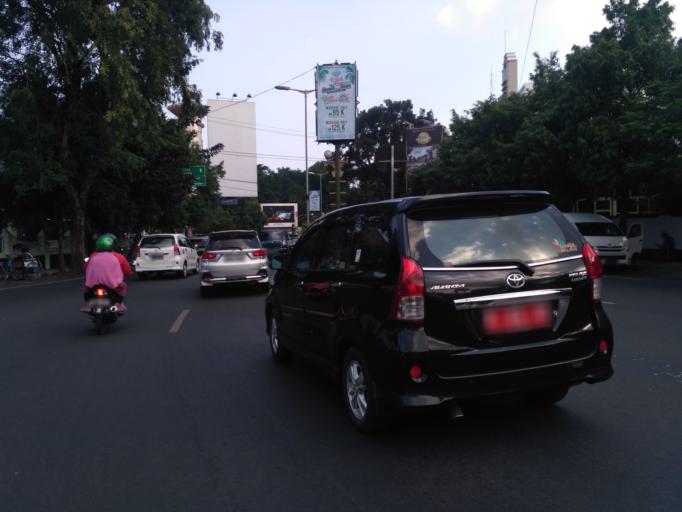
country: ID
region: East Java
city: Malang
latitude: -7.9805
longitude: 112.6305
